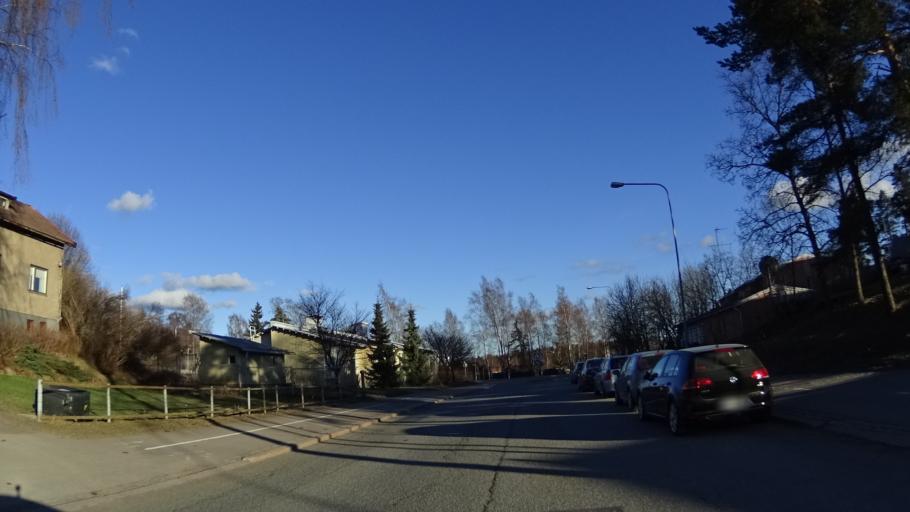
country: FI
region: Uusimaa
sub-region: Helsinki
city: Helsinki
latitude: 60.2500
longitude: 24.9574
